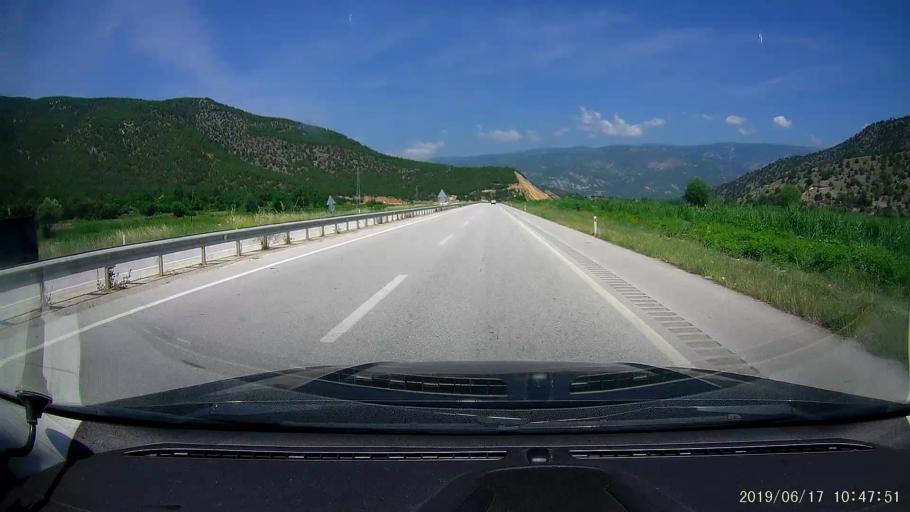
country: TR
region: Corum
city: Hacihamza
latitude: 41.0812
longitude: 34.4410
